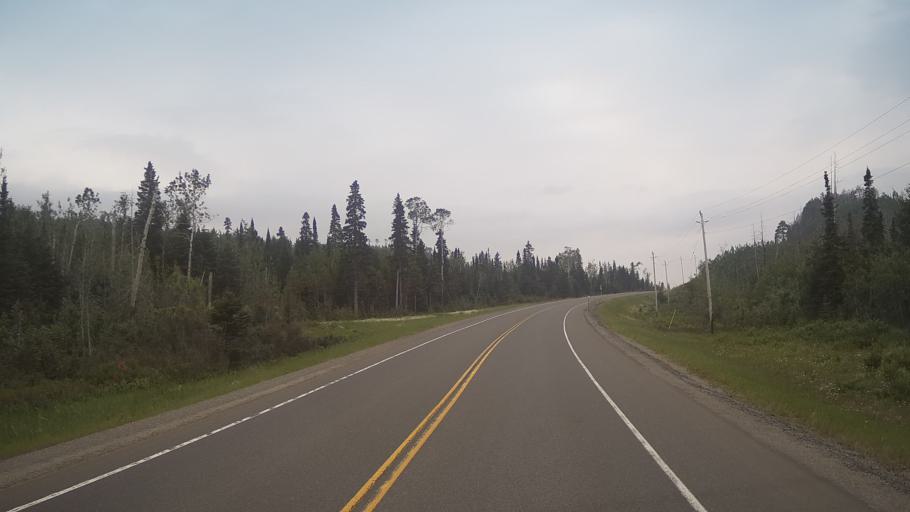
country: CA
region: Ontario
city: Greenstone
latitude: 49.4711
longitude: -88.0947
